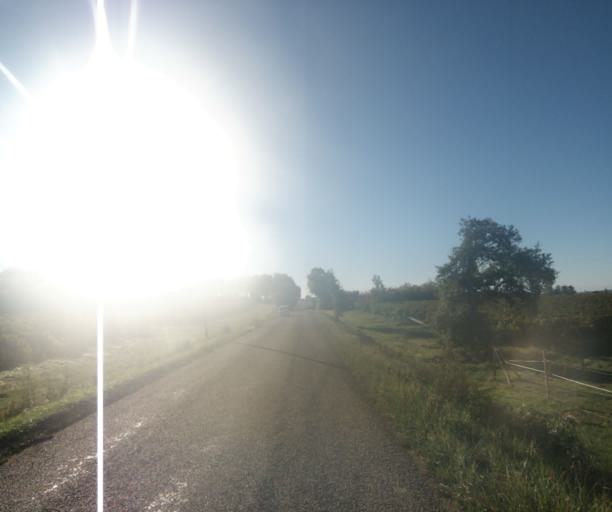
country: FR
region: Midi-Pyrenees
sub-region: Departement du Gers
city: Gondrin
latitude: 43.8543
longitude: 0.2457
